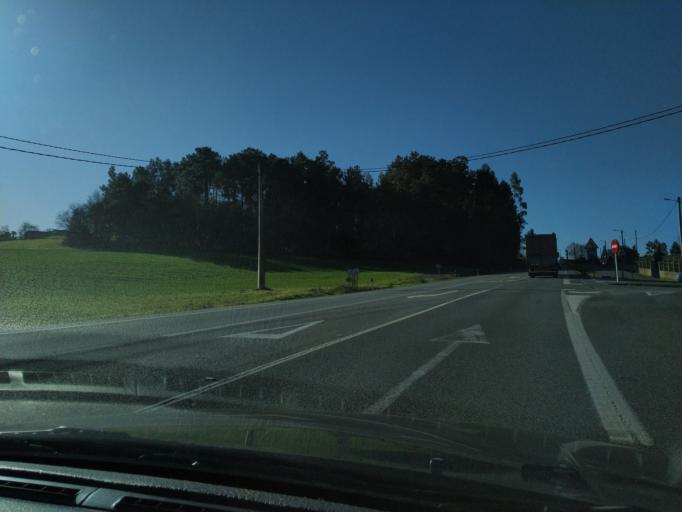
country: ES
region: Galicia
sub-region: Provincia da Coruna
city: Vedra
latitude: 42.8032
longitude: -8.4766
